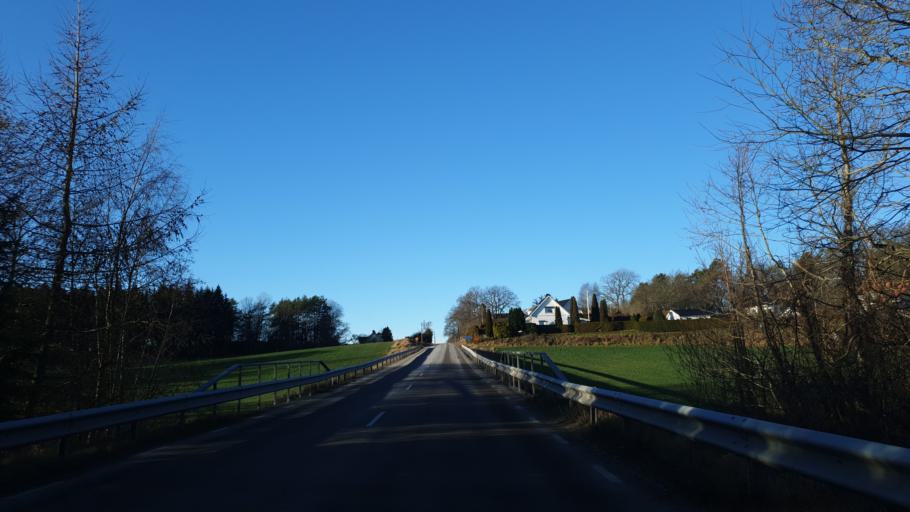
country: SE
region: Blekinge
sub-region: Ronneby Kommun
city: Ronneby
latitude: 56.1961
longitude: 15.3361
